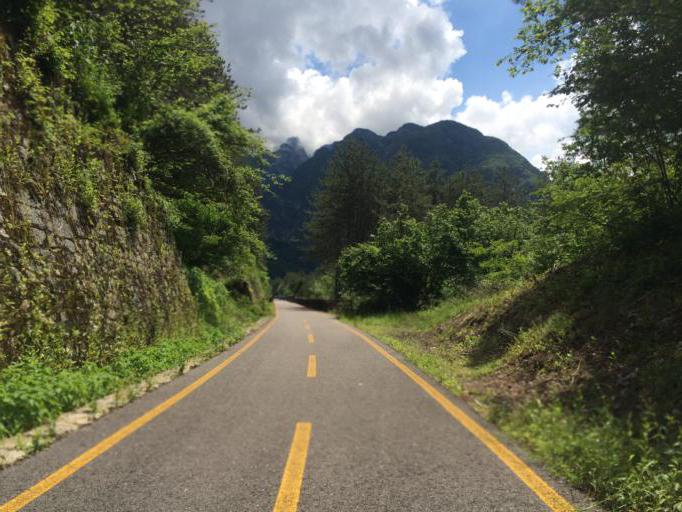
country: IT
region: Friuli Venezia Giulia
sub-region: Provincia di Udine
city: Dogna
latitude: 46.4589
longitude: 13.3049
